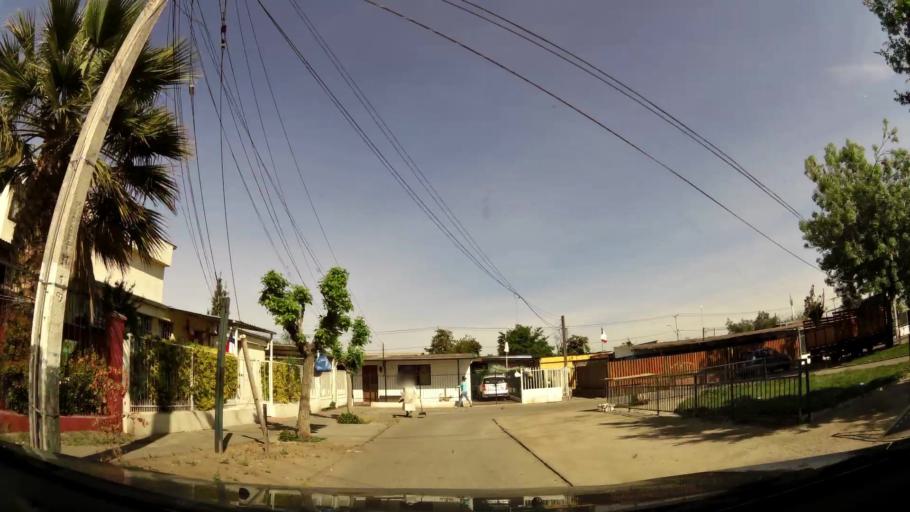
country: CL
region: Santiago Metropolitan
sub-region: Provincia de Cordillera
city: Puente Alto
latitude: -33.6054
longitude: -70.5897
